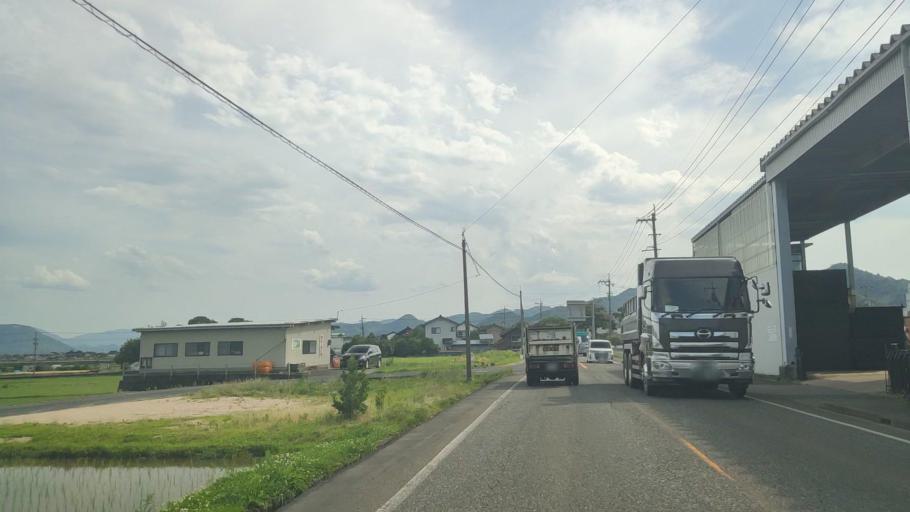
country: JP
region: Tottori
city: Tottori
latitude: 35.4790
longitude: 134.2068
